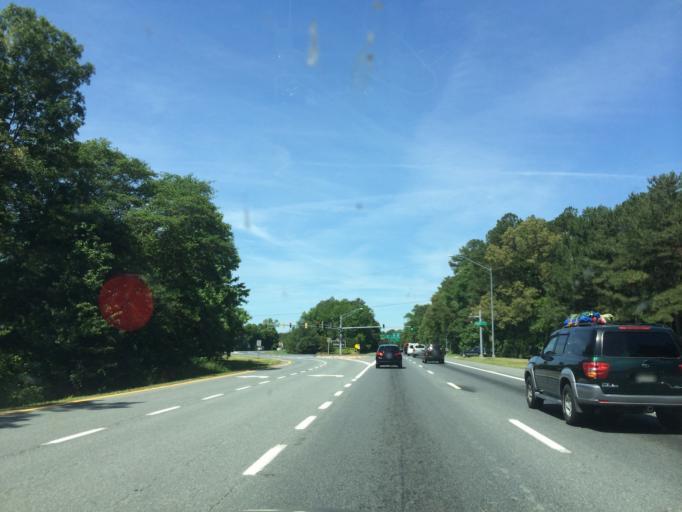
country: US
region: Maryland
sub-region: Wicomico County
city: Salisbury
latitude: 38.3722
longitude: -75.5261
